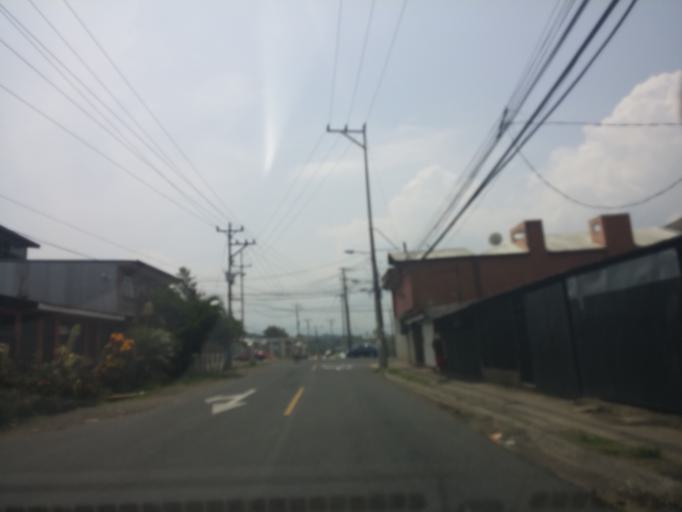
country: CR
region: Heredia
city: San Francisco
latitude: 9.9820
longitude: -84.1192
